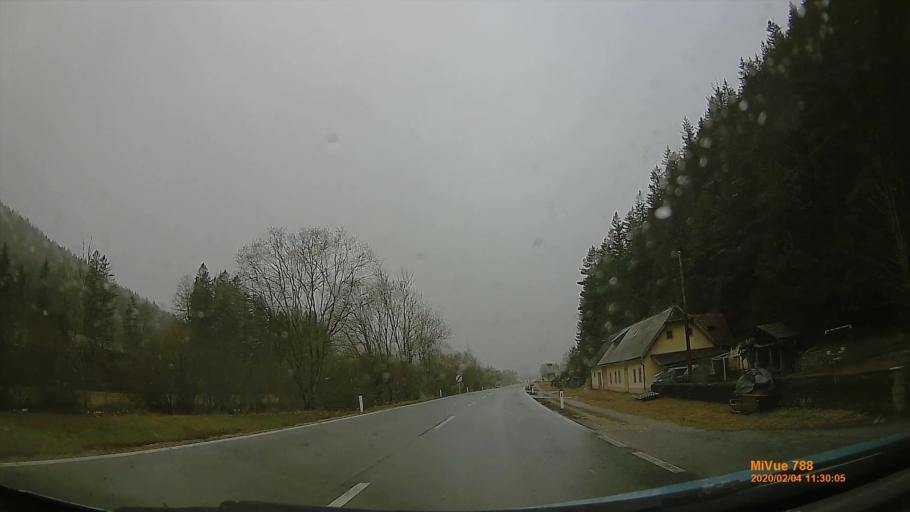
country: AT
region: Styria
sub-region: Politischer Bezirk Bruck-Muerzzuschlag
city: Kapellen
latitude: 47.6541
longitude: 15.6068
